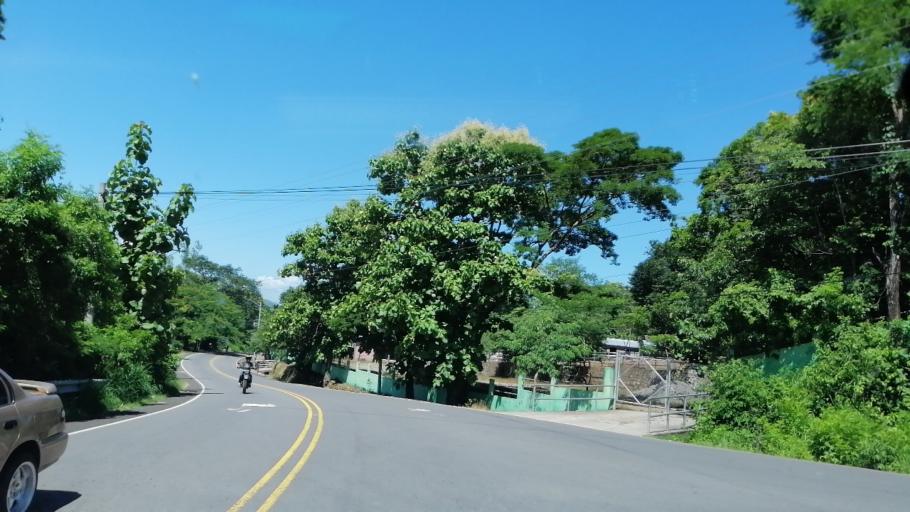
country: SV
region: Morazan
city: Cacaopera
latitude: 13.8069
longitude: -88.1498
